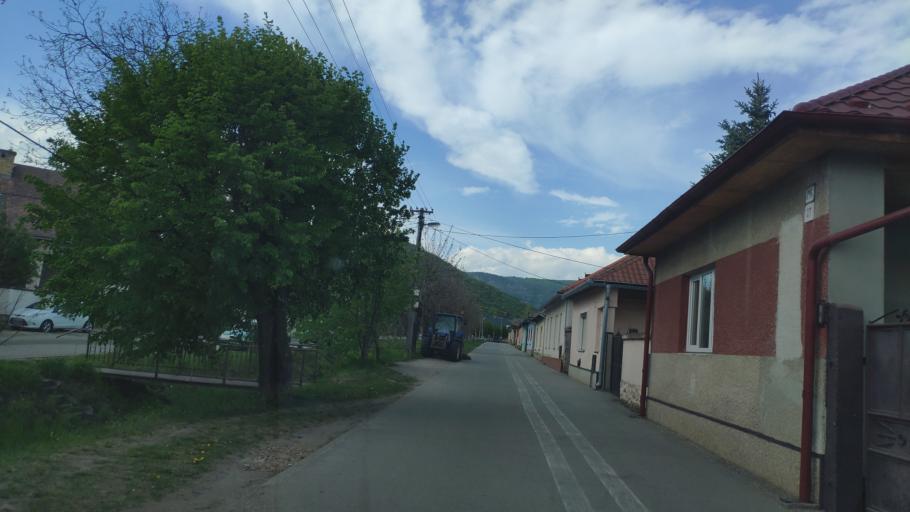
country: SK
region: Kosicky
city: Medzev
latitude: 48.5986
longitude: 20.8782
